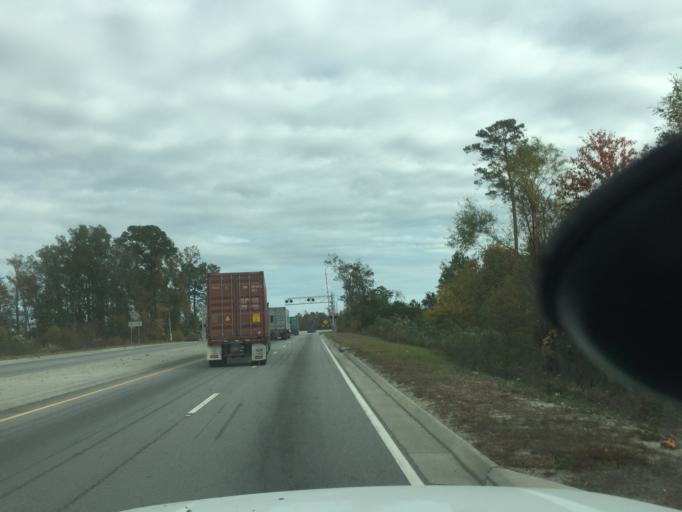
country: US
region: Georgia
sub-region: Chatham County
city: Garden City
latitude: 32.1246
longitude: -81.1834
